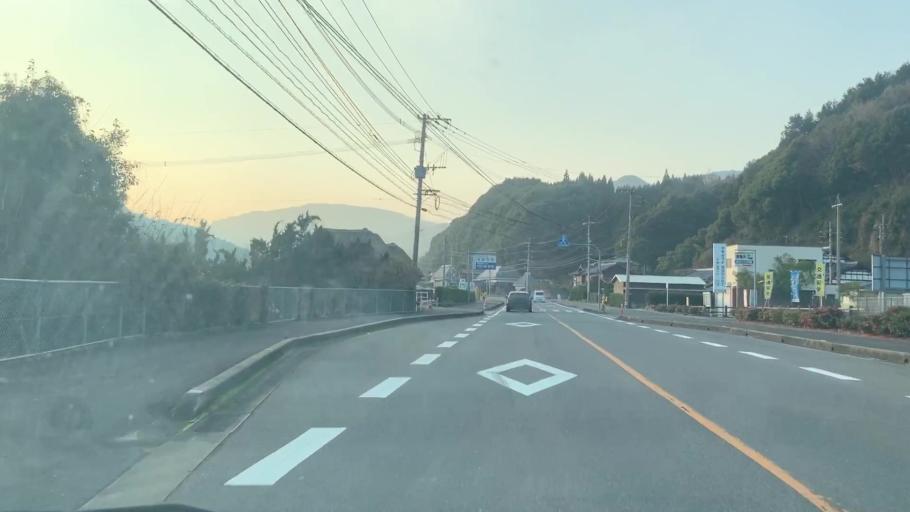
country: JP
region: Saga Prefecture
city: Takeocho-takeo
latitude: 33.2638
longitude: 130.0537
